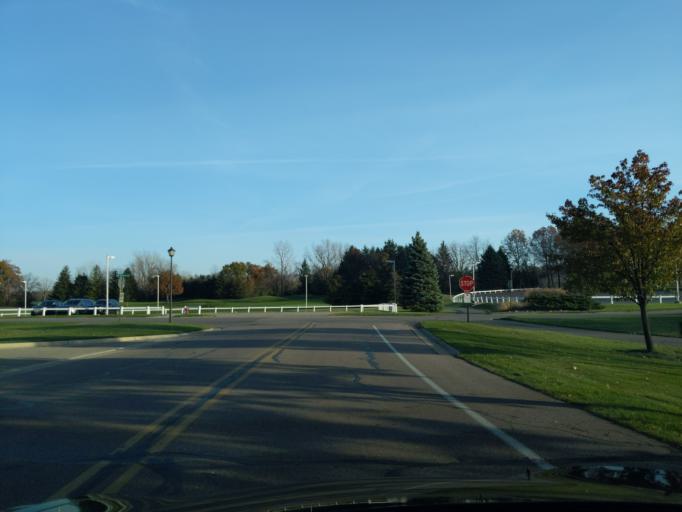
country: US
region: Michigan
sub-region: Clinton County
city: Bath
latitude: 42.7962
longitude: -84.4736
